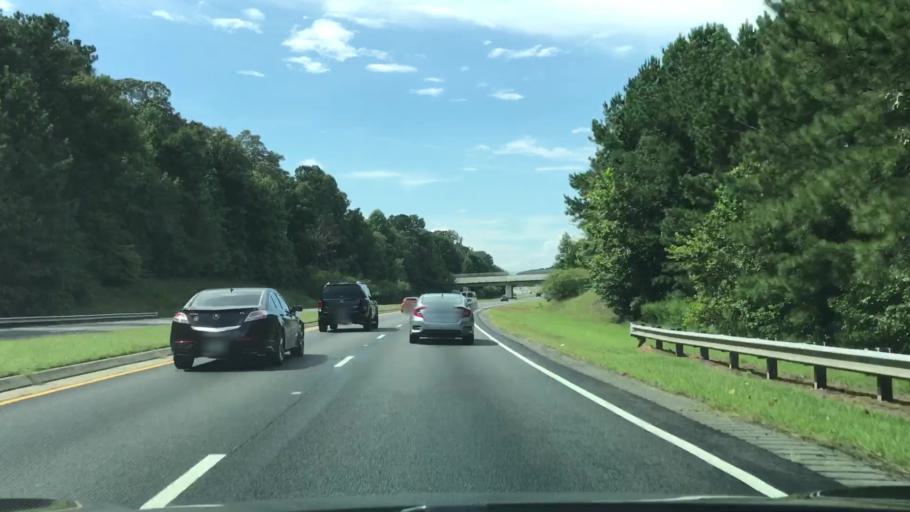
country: US
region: Georgia
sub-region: Gwinnett County
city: Lilburn
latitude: 33.8996
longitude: -84.0746
